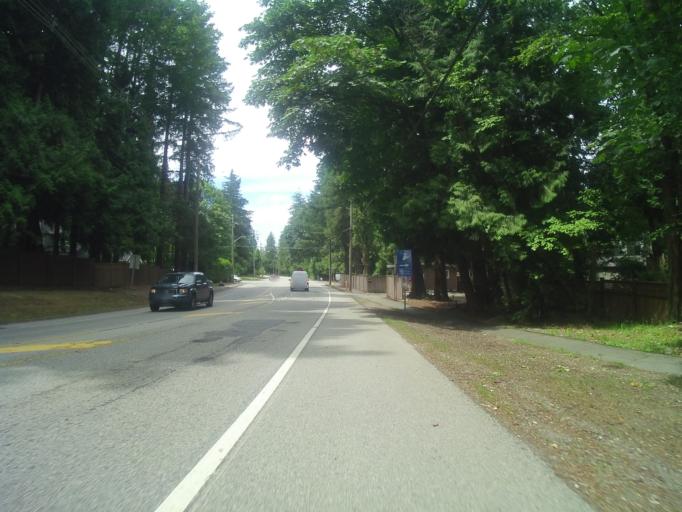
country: CA
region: British Columbia
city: Surrey
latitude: 49.0675
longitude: -122.8327
